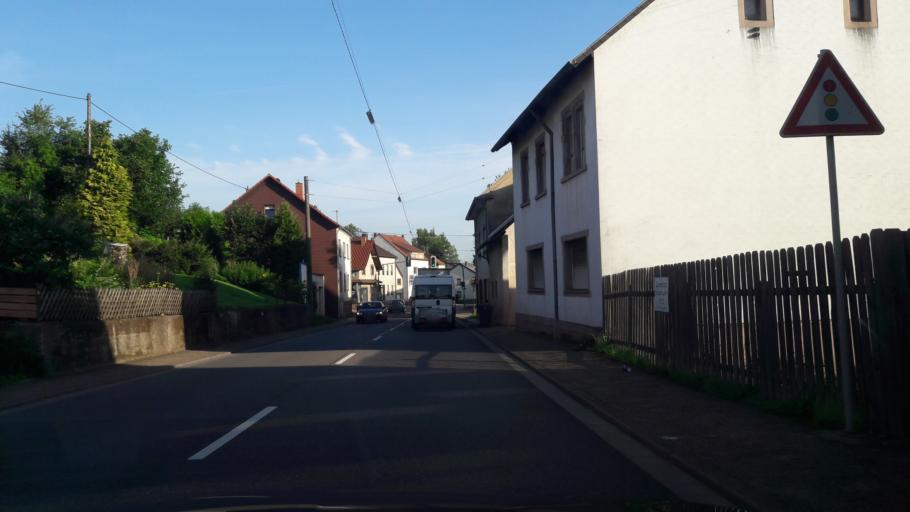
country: DE
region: Saarland
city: Lebach
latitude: 49.3892
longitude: 6.9248
